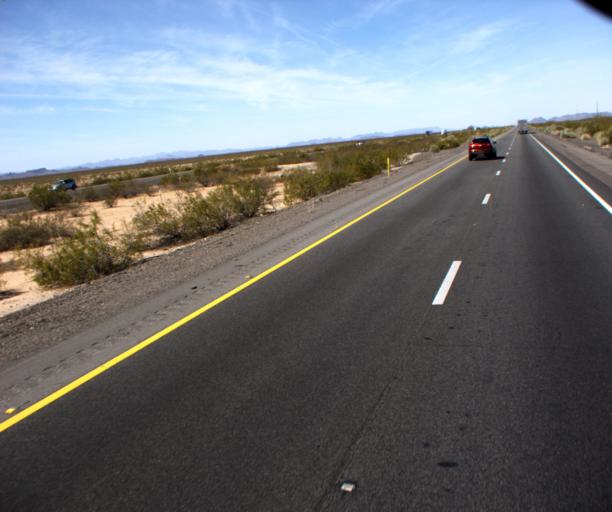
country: US
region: Arizona
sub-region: La Paz County
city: Salome
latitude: 33.5821
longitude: -113.4381
